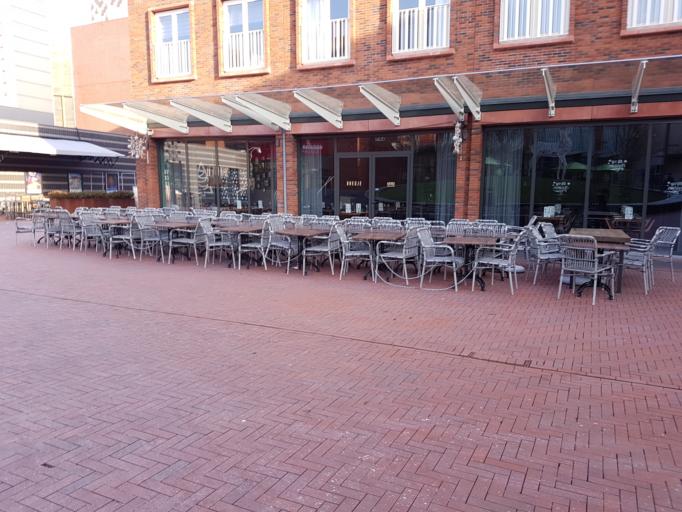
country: NL
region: South Holland
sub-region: Gemeente Zoetermeer
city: Zoetermeer
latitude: 52.0619
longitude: 4.4941
